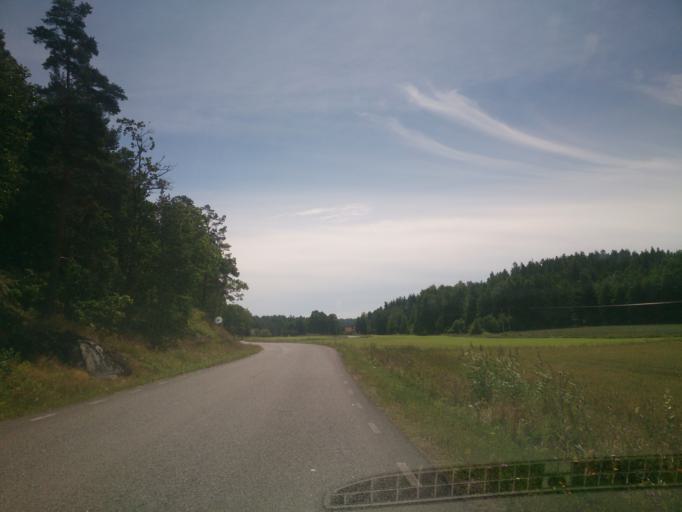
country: SE
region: OEstergoetland
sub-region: Valdemarsviks Kommun
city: Valdemarsvik
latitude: 58.2810
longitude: 16.6882
